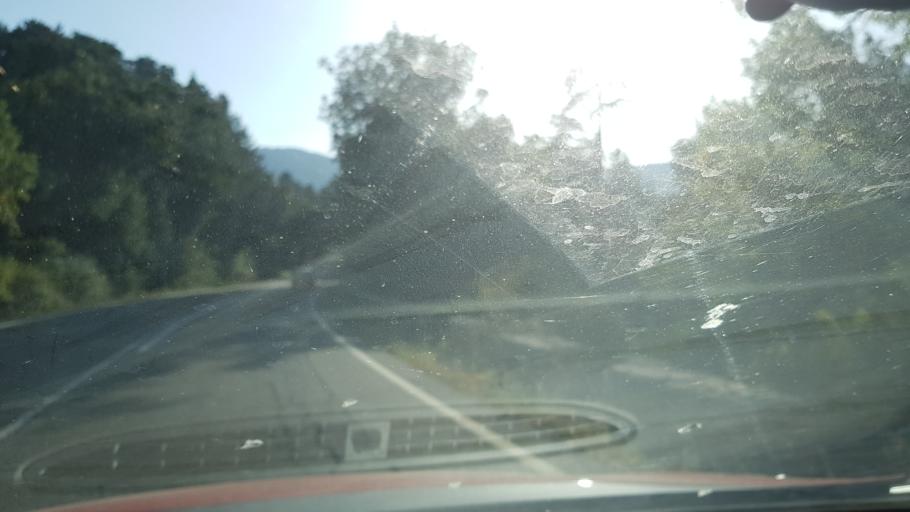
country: ES
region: Castille and Leon
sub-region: Provincia de Segovia
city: San Ildefonso
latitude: 40.8679
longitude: -4.0235
